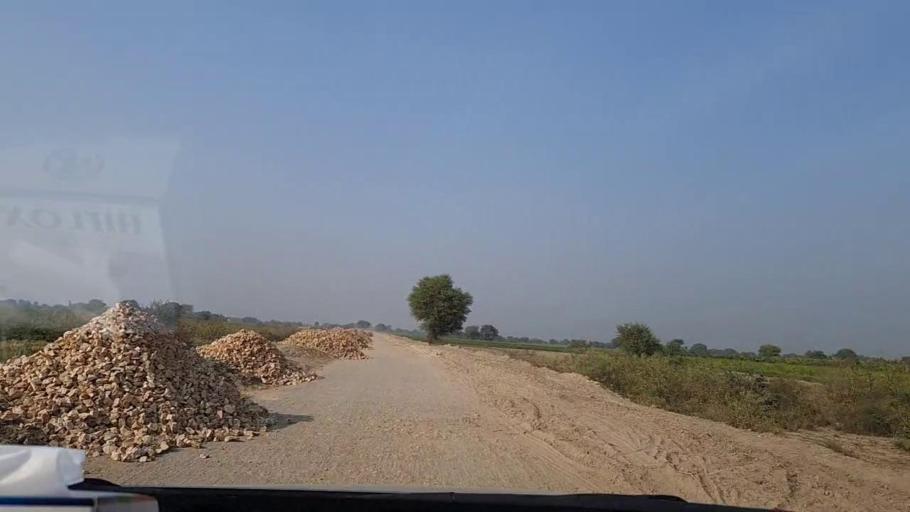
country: PK
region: Sindh
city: Tando Ghulam Ali
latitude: 25.1669
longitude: 68.8784
